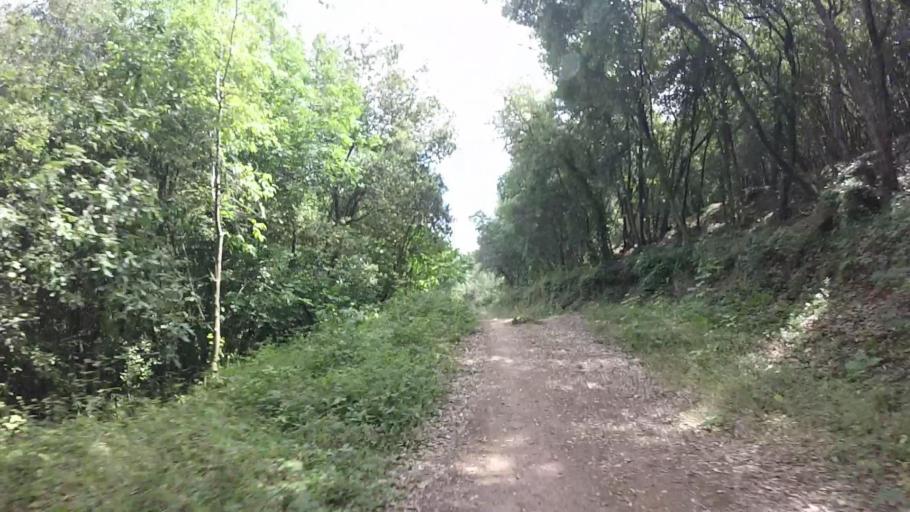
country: FR
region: Provence-Alpes-Cote d'Azur
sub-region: Departement des Alpes-Maritimes
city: Biot
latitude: 43.6169
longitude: 7.0868
